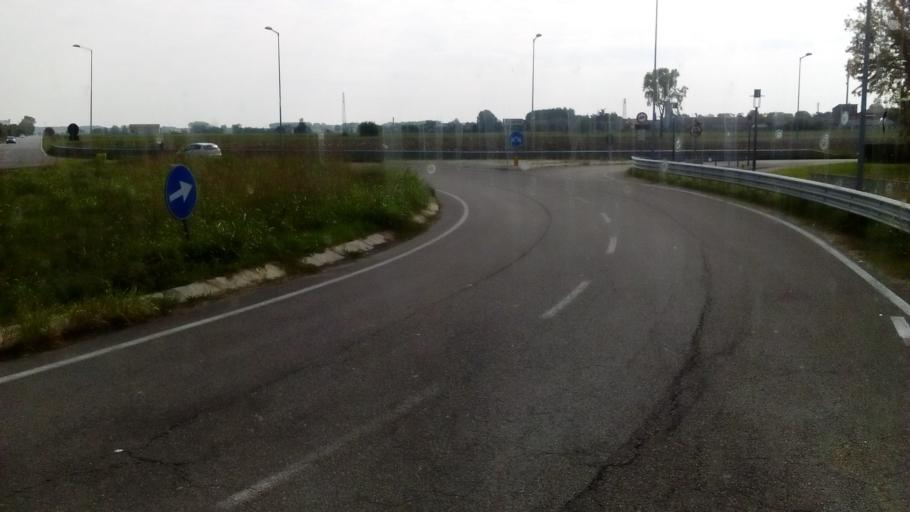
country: IT
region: Veneto
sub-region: Provincia di Rovigo
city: Calto
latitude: 44.9960
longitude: 11.3608
